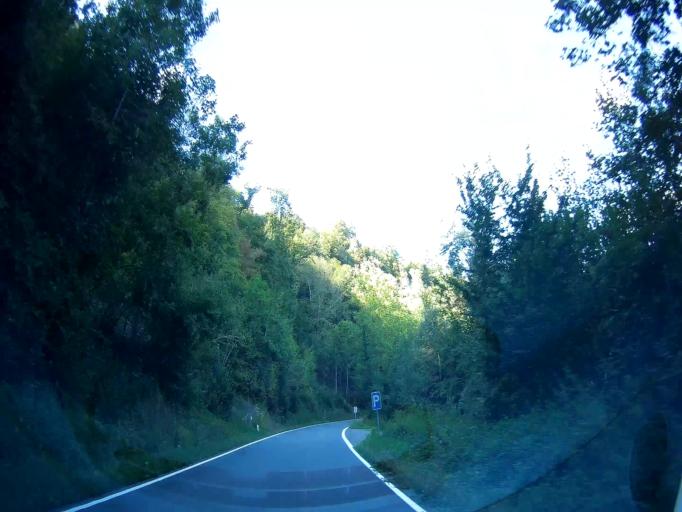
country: BE
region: Wallonia
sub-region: Province de Namur
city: Onhaye
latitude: 50.2973
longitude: 4.8143
